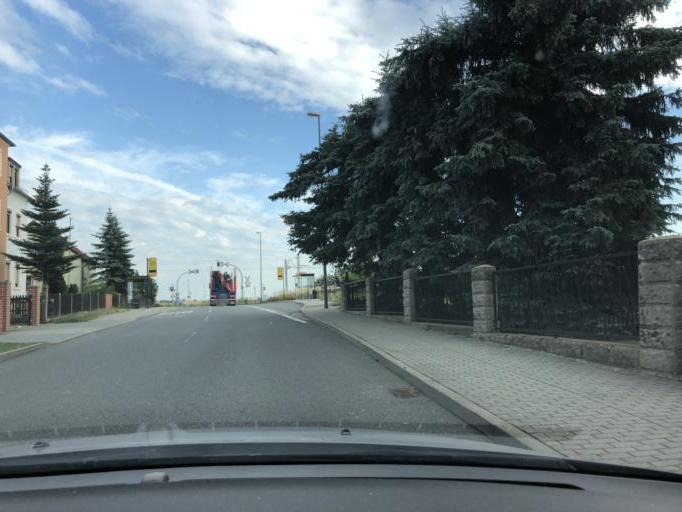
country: DE
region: Saxony
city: Freital
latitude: 51.0415
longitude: 13.6253
